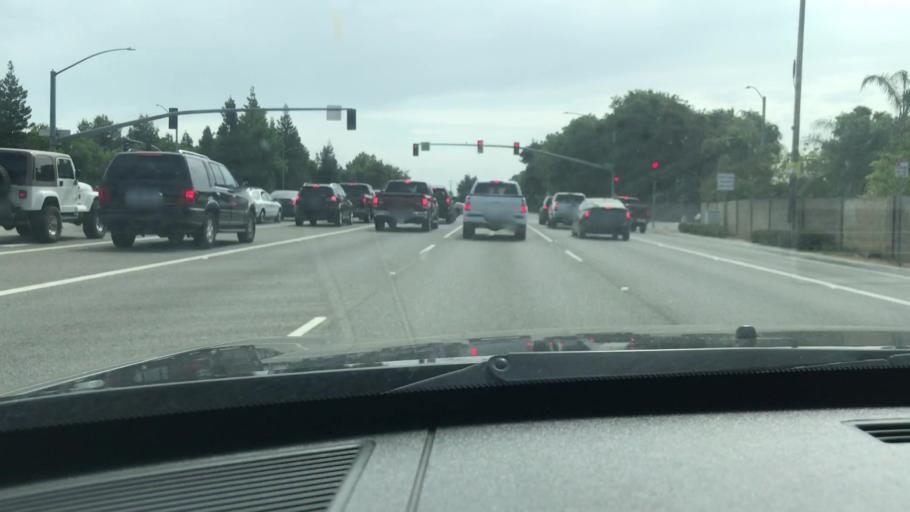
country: US
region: California
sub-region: Fresno County
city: Clovis
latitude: 36.8375
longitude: -119.7370
